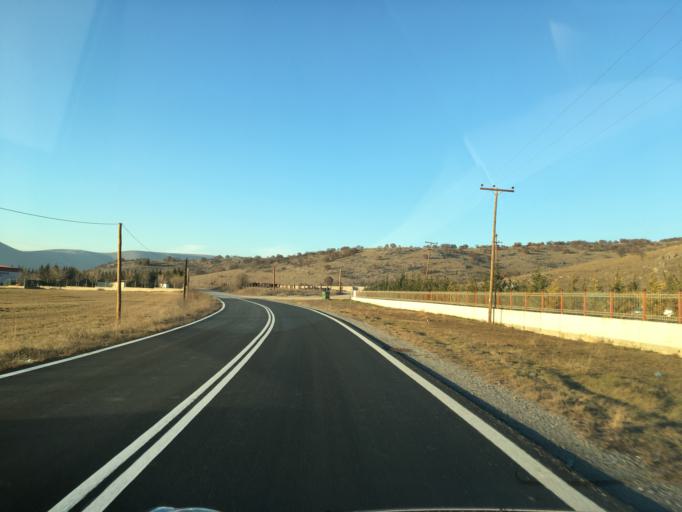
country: GR
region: West Macedonia
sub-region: Nomos Kozanis
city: Kozani
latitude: 40.3026
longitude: 21.7363
